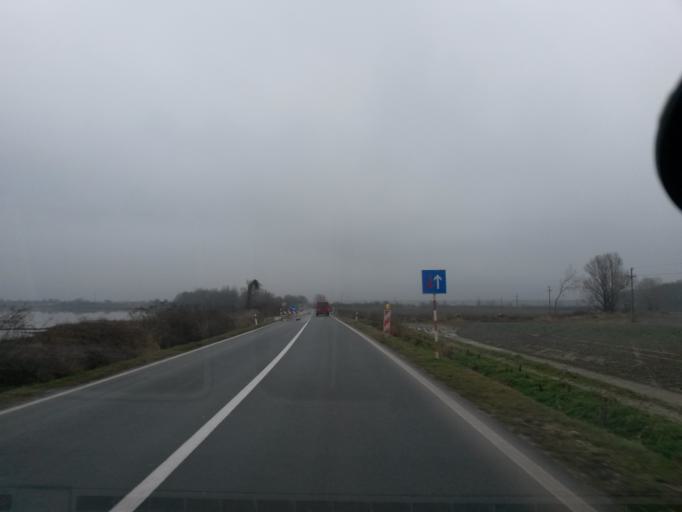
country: HR
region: Vukovarsko-Srijemska
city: Drenovci
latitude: 44.9279
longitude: 18.8190
